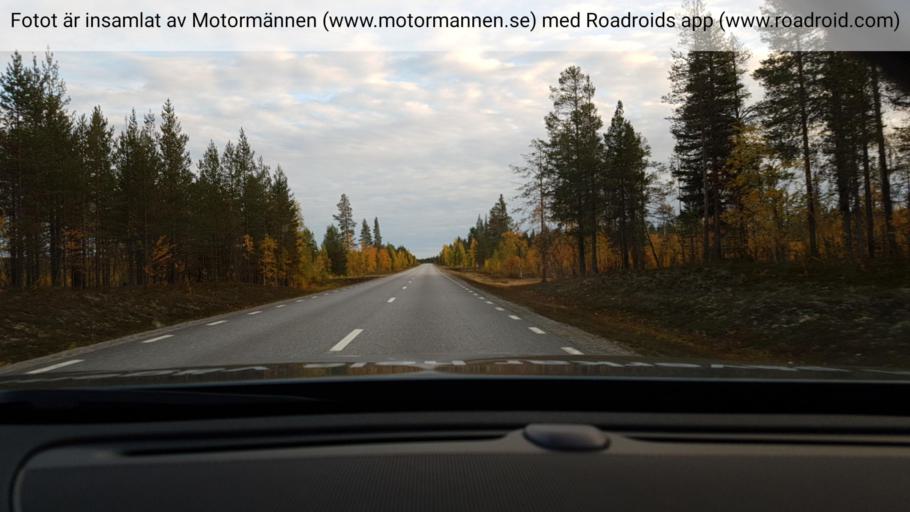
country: SE
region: Norrbotten
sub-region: Jokkmokks Kommun
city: Jokkmokk
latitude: 66.4144
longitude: 19.6881
